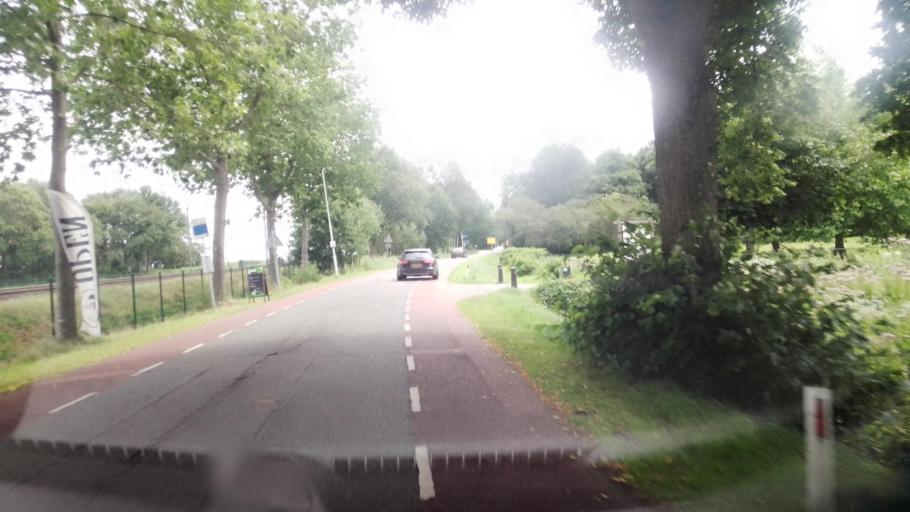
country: NL
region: Limburg
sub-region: Gemeente Venray
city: Venray
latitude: 51.4463
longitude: 5.8725
